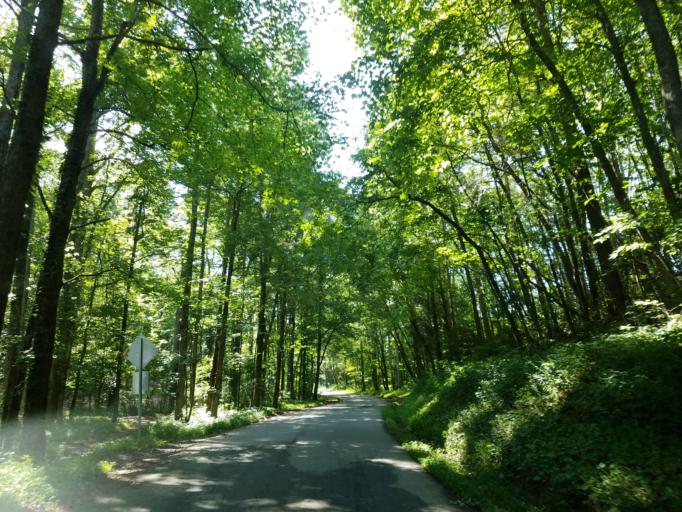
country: US
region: Georgia
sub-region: Dawson County
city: Dawsonville
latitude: 34.5709
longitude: -84.1539
